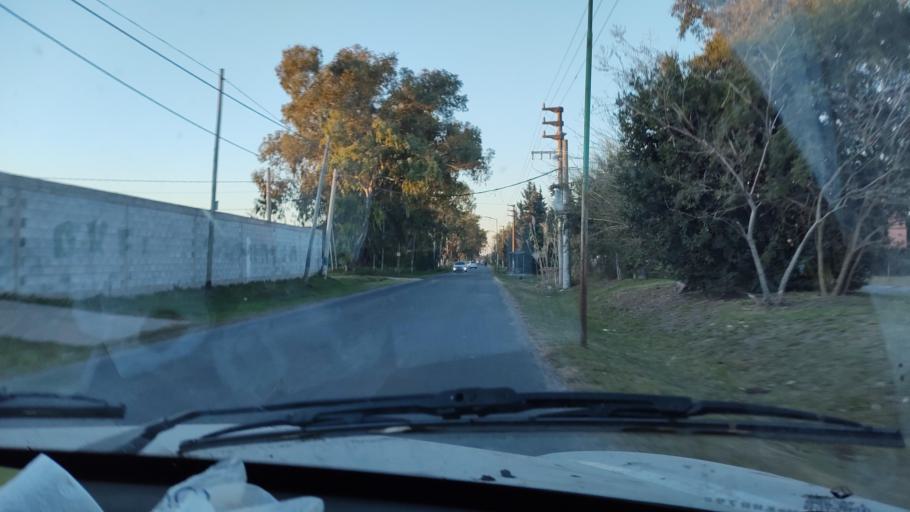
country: AR
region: Buenos Aires
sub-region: Partido de La Plata
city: La Plata
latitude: -34.9058
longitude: -58.0330
